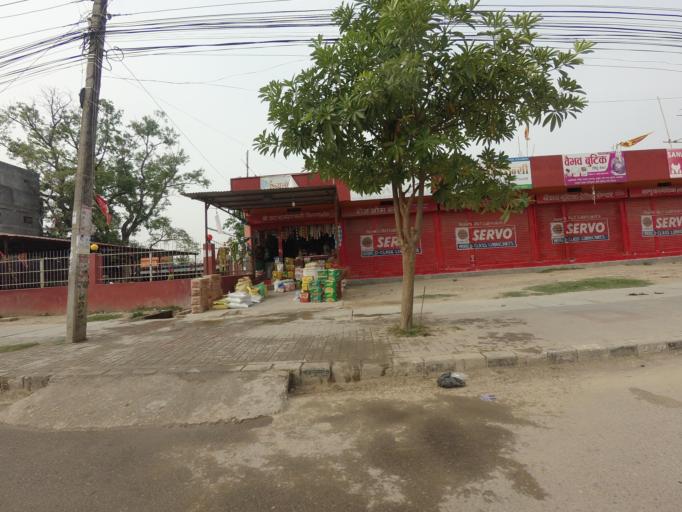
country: NP
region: Western Region
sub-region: Lumbini Zone
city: Bhairahawa
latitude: 27.5082
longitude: 83.4372
